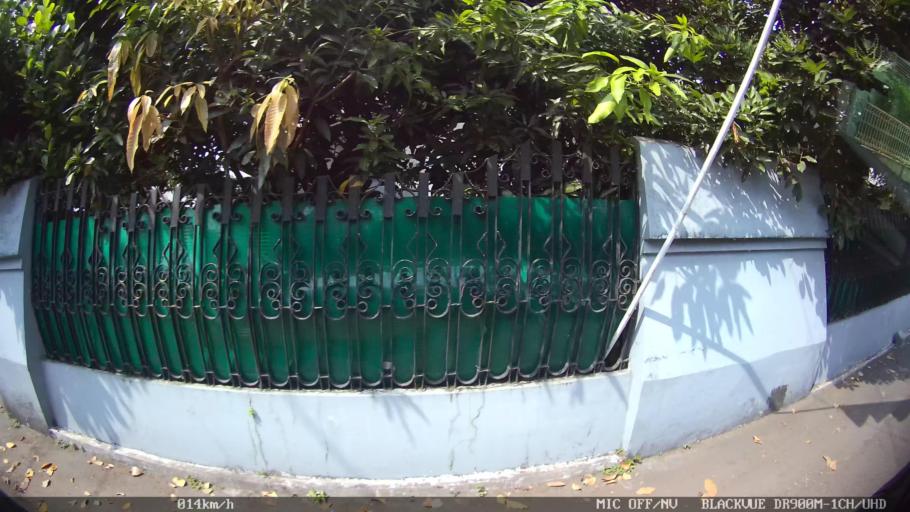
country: ID
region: Daerah Istimewa Yogyakarta
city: Yogyakarta
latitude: -7.8131
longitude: 110.3814
